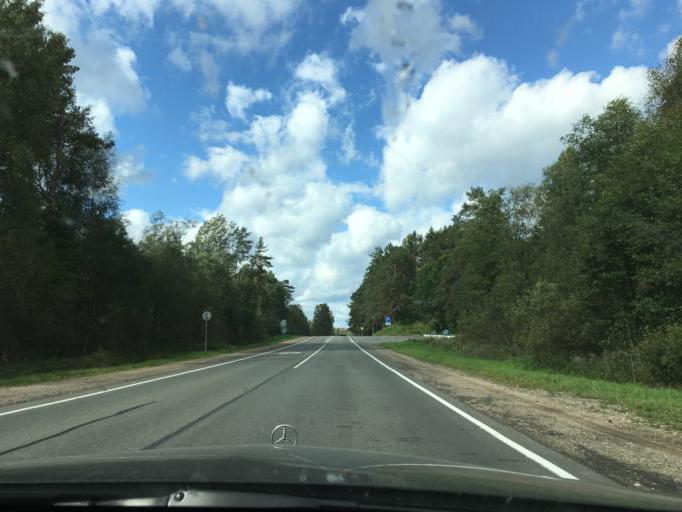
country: RU
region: Pskov
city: Pustoshka
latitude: 56.3898
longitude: 29.2496
